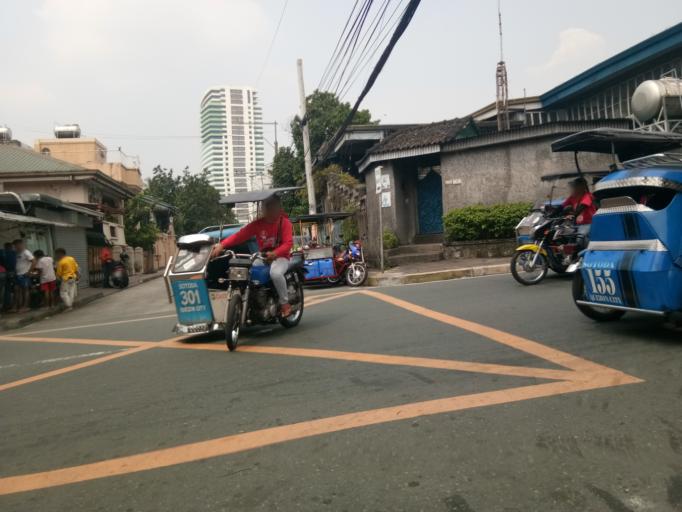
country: PH
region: Metro Manila
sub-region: San Juan
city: San Juan
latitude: 14.6143
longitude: 121.0559
